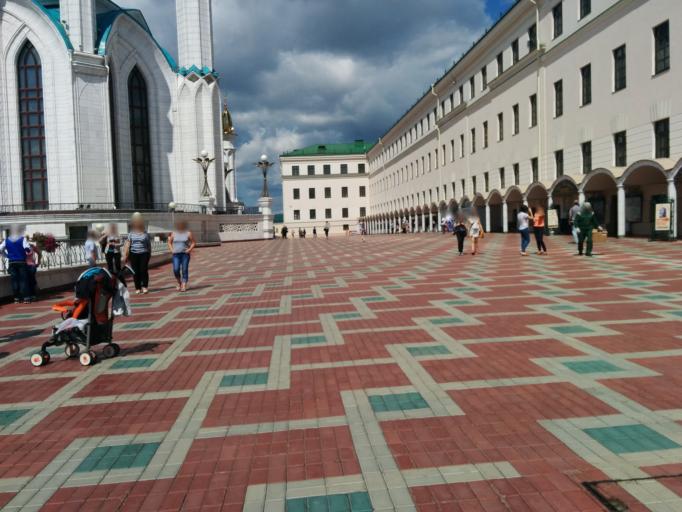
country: RU
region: Tatarstan
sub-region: Gorod Kazan'
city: Kazan
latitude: 55.7980
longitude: 49.1061
